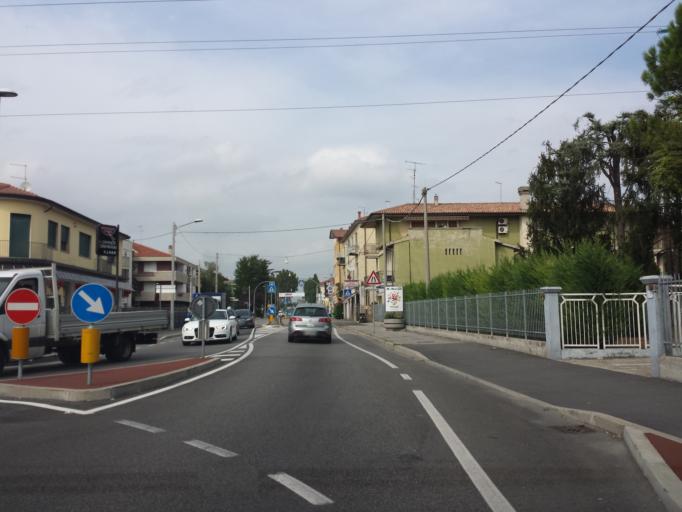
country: IT
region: Veneto
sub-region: Provincia di Padova
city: Vigodarzere
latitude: 45.4420
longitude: 11.8934
